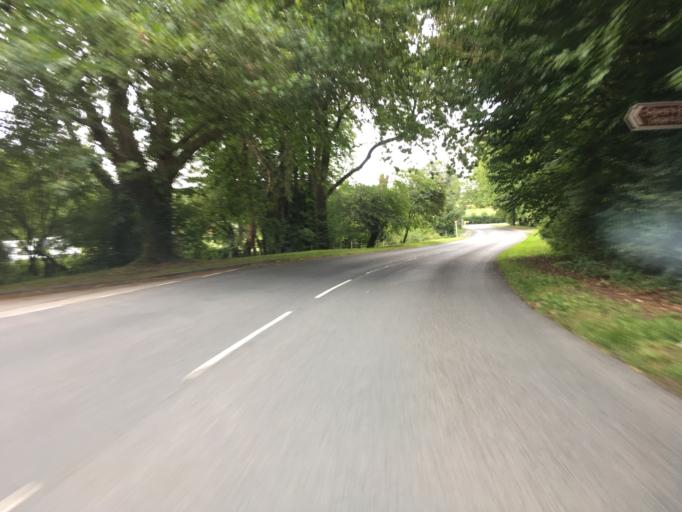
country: GB
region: England
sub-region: Hampshire
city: Kings Worthy
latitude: 51.0875
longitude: -1.3058
